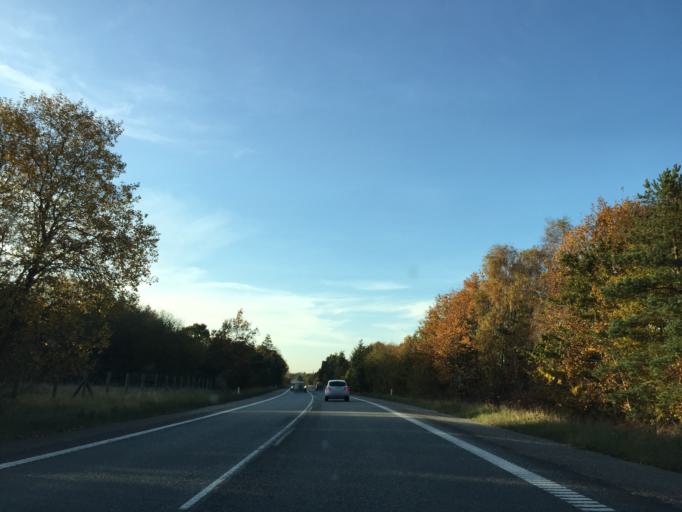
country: DK
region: South Denmark
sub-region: Aabenraa Kommune
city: Krusa
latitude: 54.8698
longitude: 9.3959
